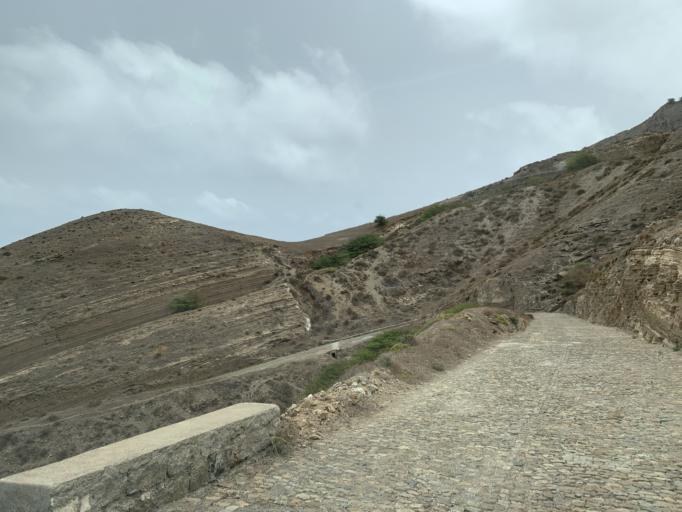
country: CV
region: Brava
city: Vila Nova Sintra
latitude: 14.8774
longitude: -24.7317
